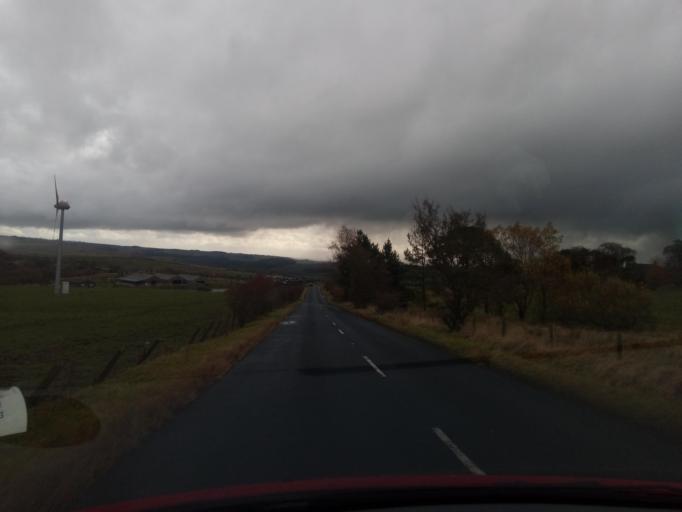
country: GB
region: England
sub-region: Northumberland
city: Corsenside
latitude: 55.1596
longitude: -2.2628
